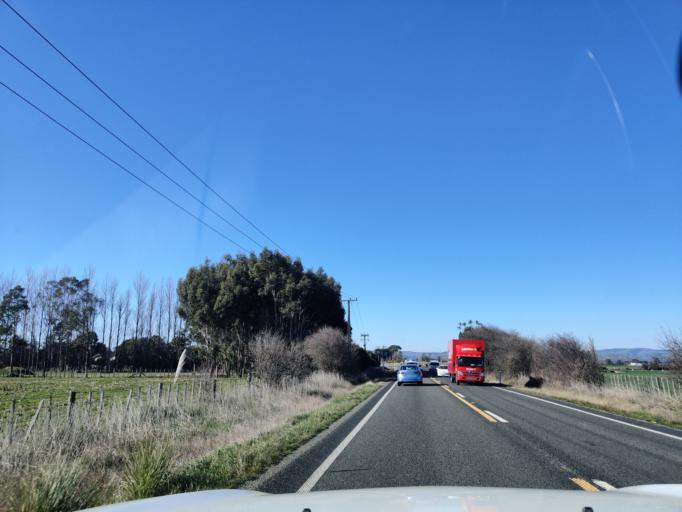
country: NZ
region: Manawatu-Wanganui
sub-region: Palmerston North City
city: Palmerston North
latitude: -40.2934
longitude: 175.5712
